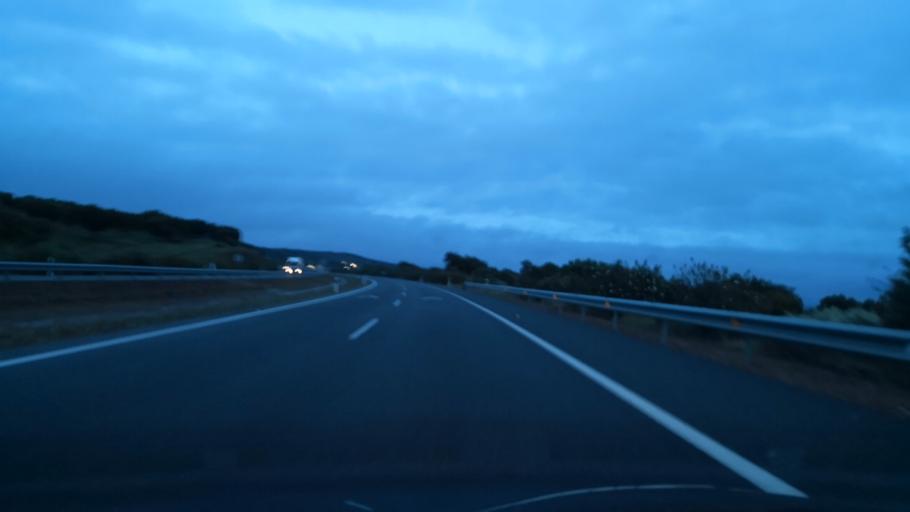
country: ES
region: Extremadura
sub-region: Provincia de Badajoz
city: Aljucen
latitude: 39.0554
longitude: -6.3251
